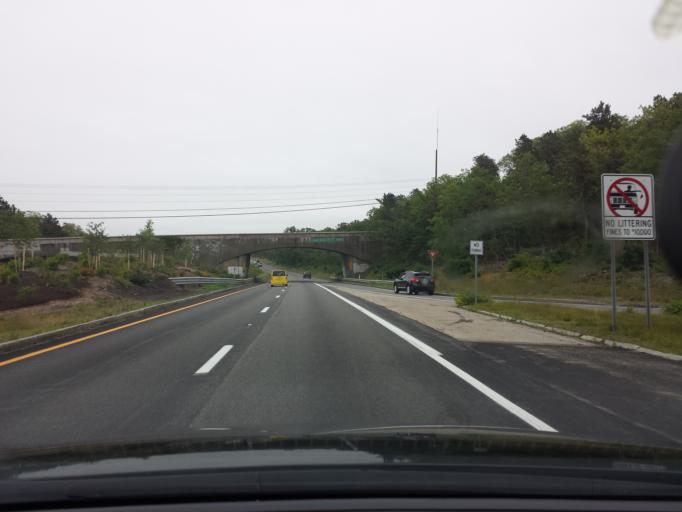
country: US
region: Massachusetts
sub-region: Barnstable County
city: East Sandwich
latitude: 41.7311
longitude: -70.4586
